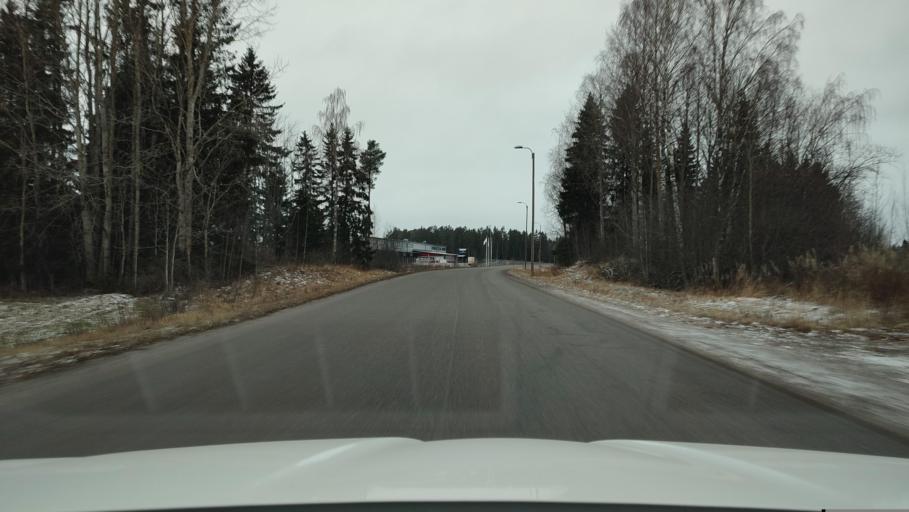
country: FI
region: Ostrobothnia
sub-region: Vaasa
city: Ristinummi
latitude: 63.0371
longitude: 21.7819
